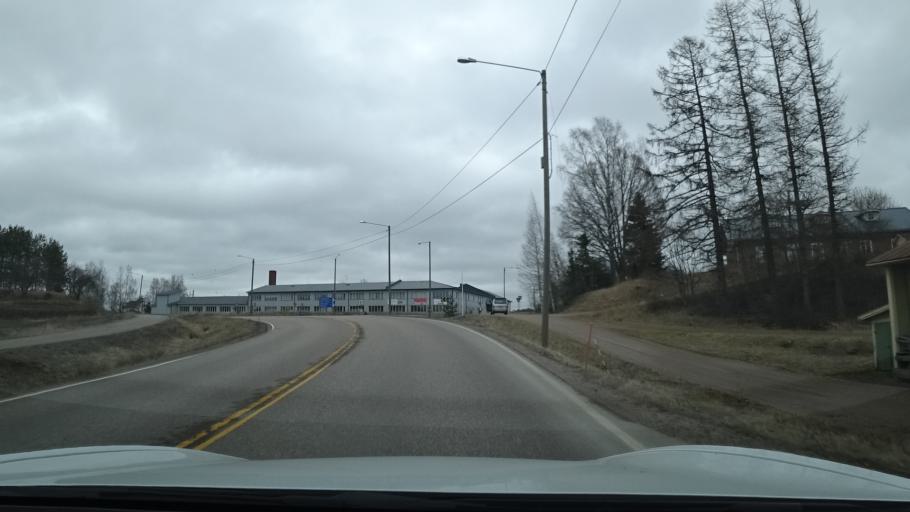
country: FI
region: Uusimaa
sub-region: Porvoo
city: Myrskylae
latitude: 60.6728
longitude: 25.8745
